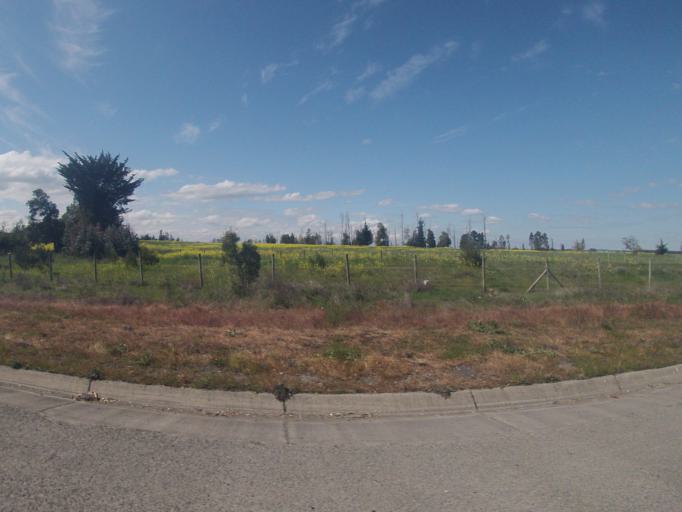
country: CL
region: Biobio
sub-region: Provincia de Biobio
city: Los Angeles
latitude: -37.4480
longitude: -72.4056
